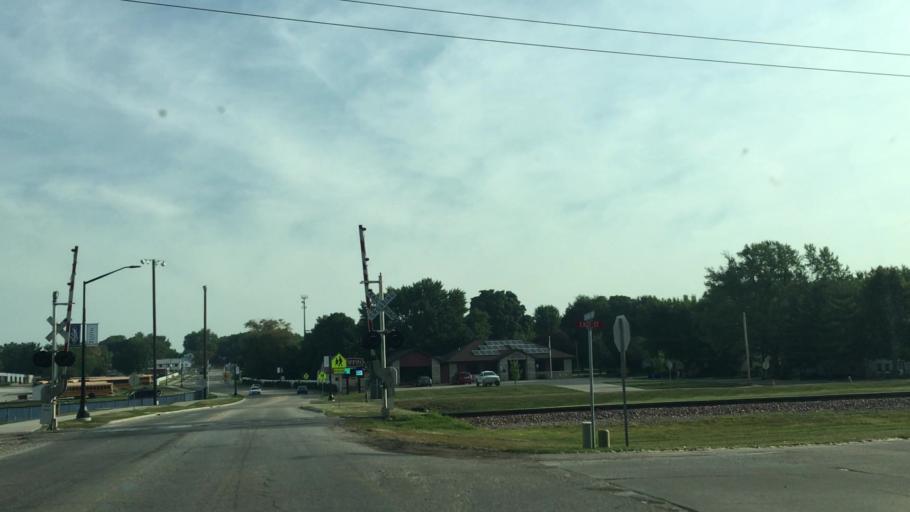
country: US
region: Iowa
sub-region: Johnson County
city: Tiffin
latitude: 41.7031
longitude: -91.6666
